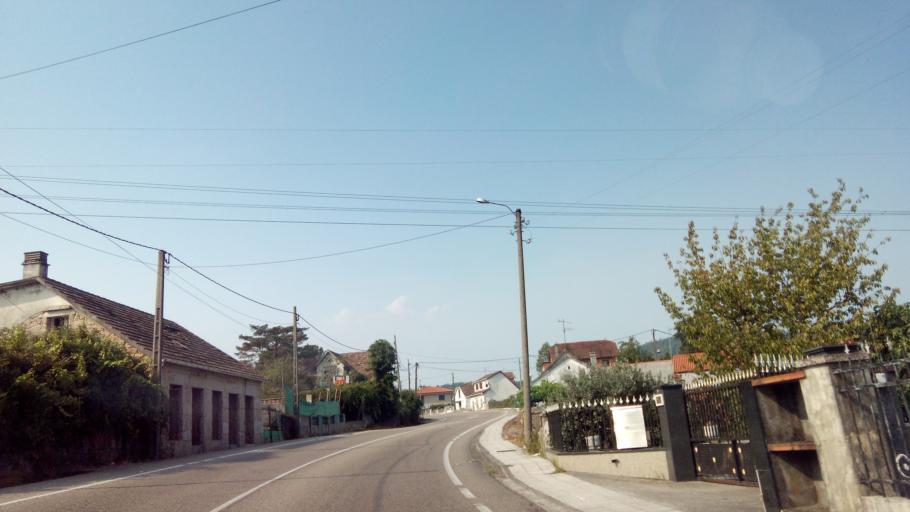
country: ES
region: Galicia
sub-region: Provincia de Pontevedra
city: Ponteareas
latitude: 42.1838
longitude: -8.5072
